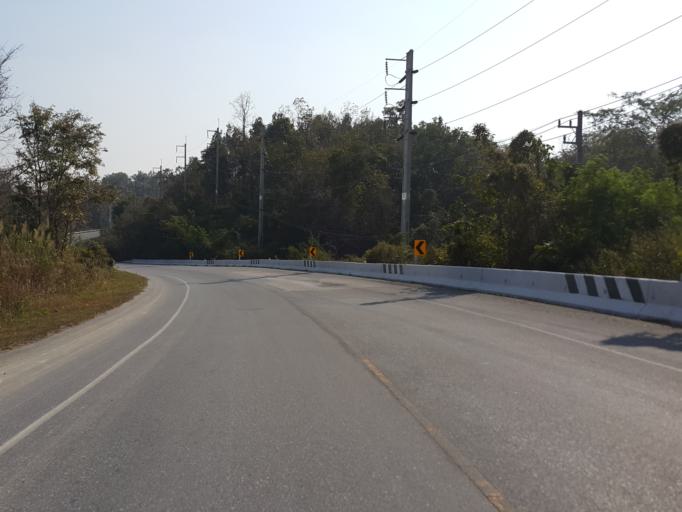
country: TH
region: Lampang
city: Chae Hom
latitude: 18.5851
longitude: 99.5519
